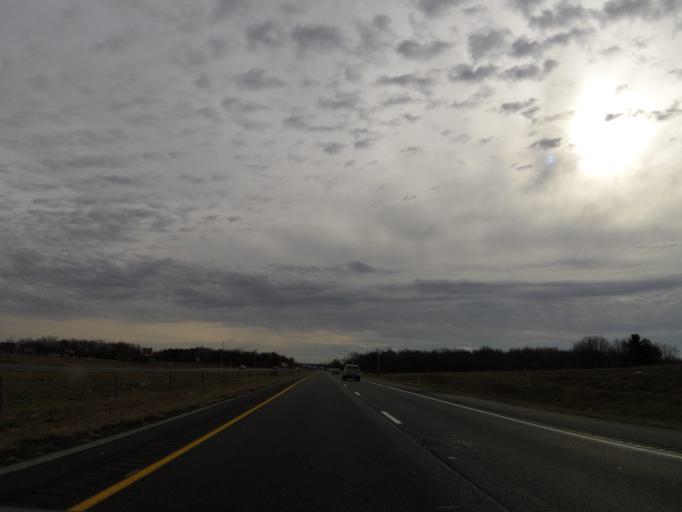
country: US
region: Indiana
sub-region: Hendricks County
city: Fairfield Heights
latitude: 39.8397
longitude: -86.3536
